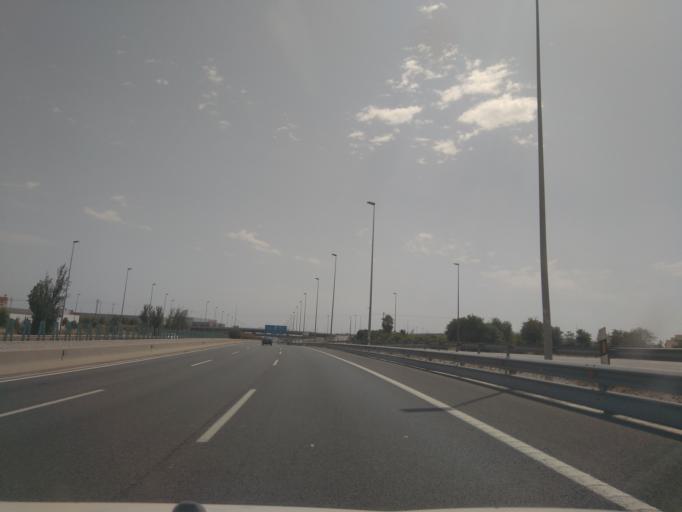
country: ES
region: Valencia
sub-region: Provincia de Valencia
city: Silla
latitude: 39.3702
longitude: -0.4265
